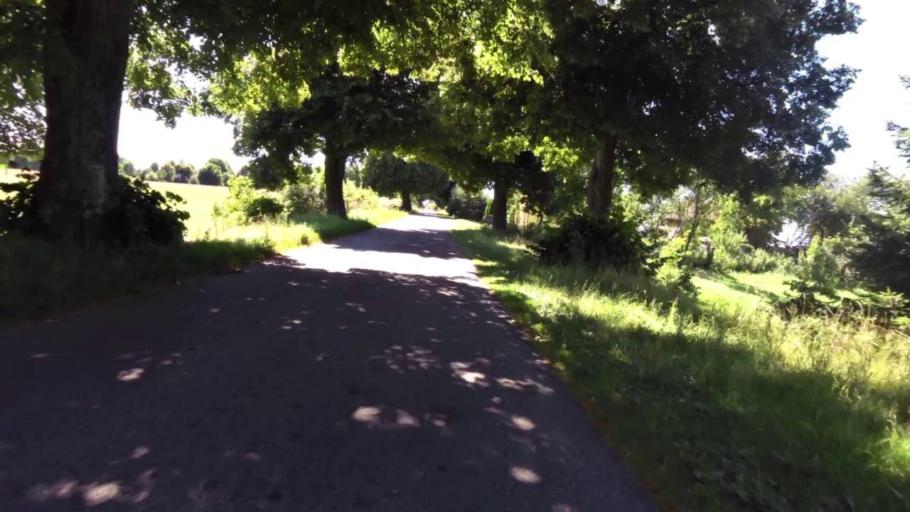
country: PL
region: West Pomeranian Voivodeship
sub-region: Powiat szczecinecki
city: Bialy Bor
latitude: 53.9277
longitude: 16.8510
